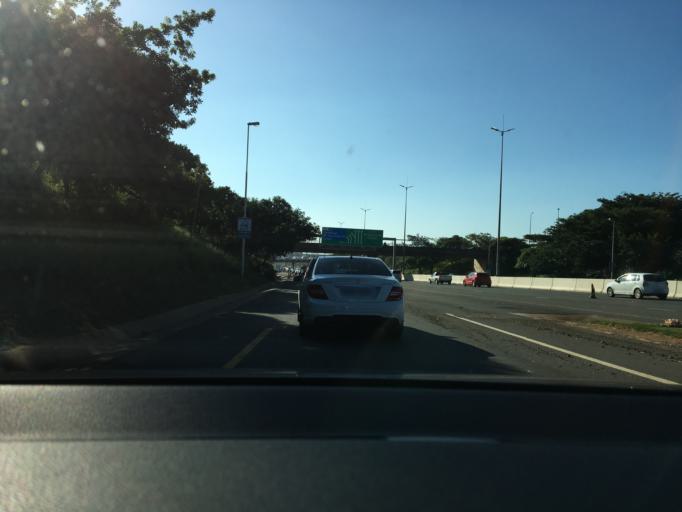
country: ZA
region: KwaZulu-Natal
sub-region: eThekwini Metropolitan Municipality
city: Durban
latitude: -29.7304
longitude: 31.0655
